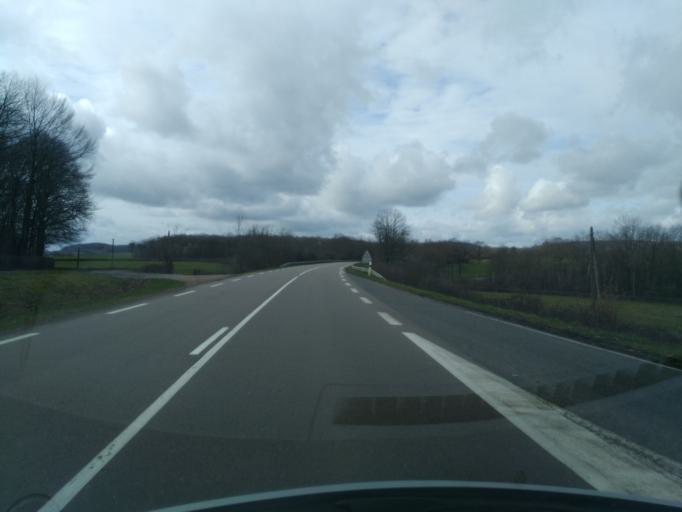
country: FR
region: Bourgogne
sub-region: Departement de Saone-et-Loire
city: Torcy
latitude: 46.7678
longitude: 4.4358
